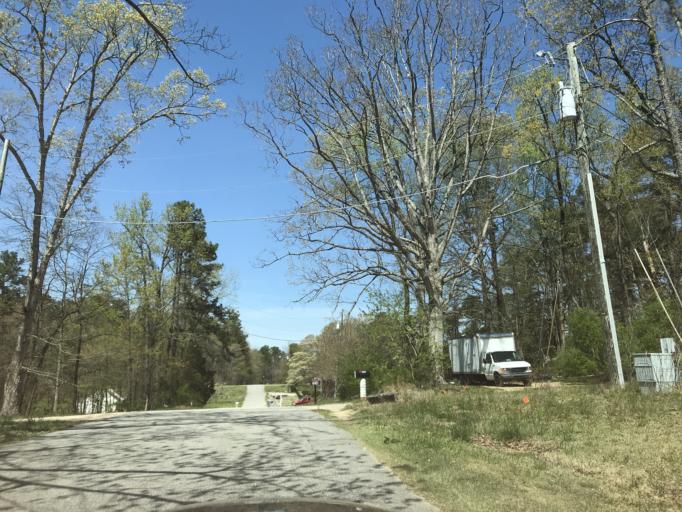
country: US
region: North Carolina
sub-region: Wake County
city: Raleigh
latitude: 35.8118
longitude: -78.5752
